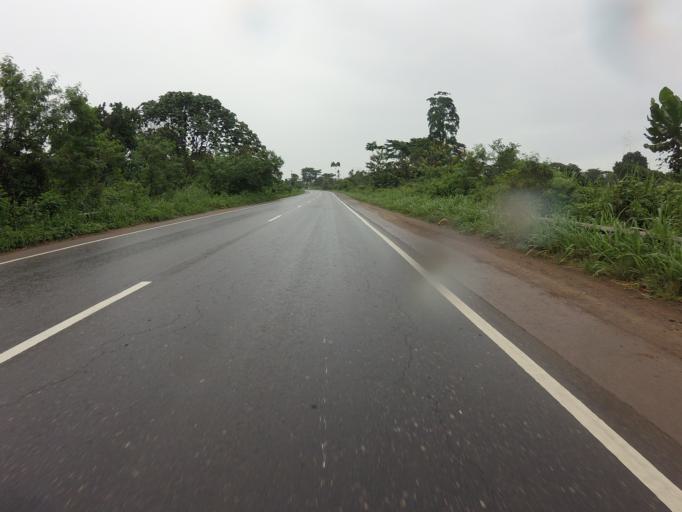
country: GH
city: Kibi
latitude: 6.1451
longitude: -0.4872
